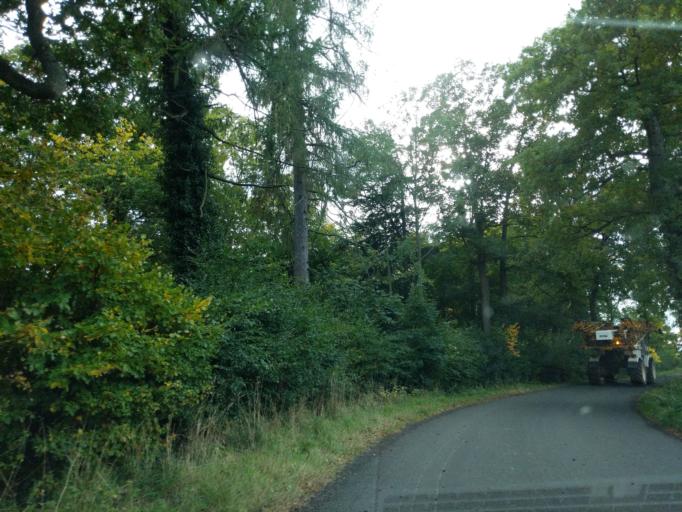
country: GB
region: Scotland
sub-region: East Lothian
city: Haddington
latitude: 55.9315
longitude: -2.7821
